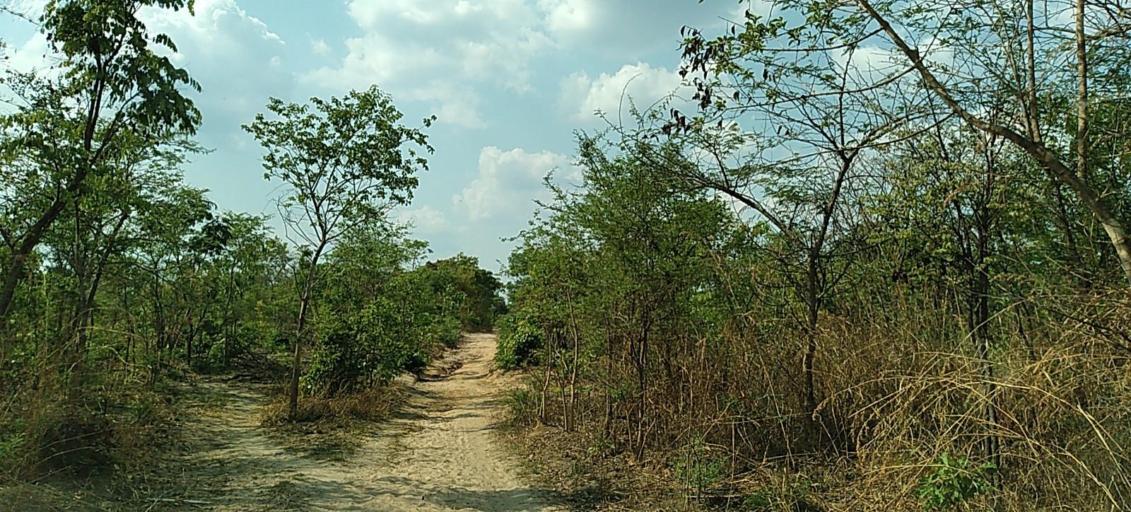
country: ZM
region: Copperbelt
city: Luanshya
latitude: -13.2212
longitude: 28.3317
